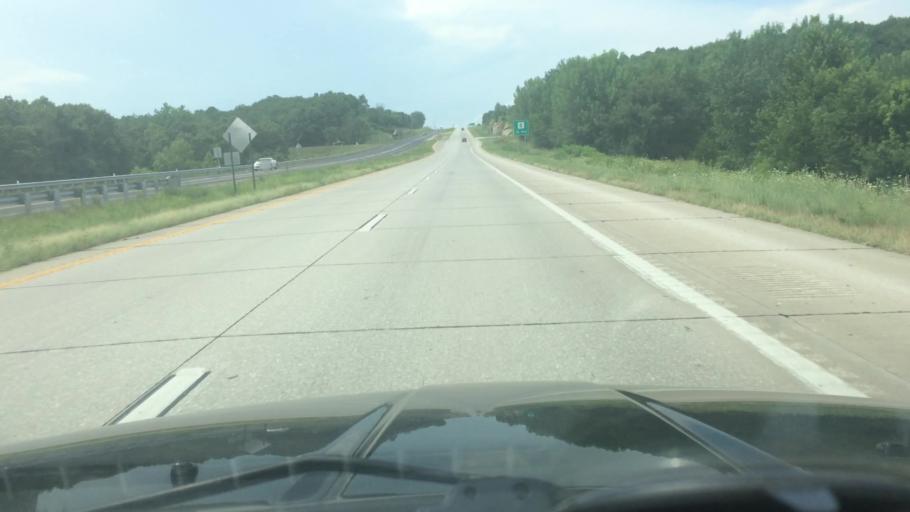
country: US
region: Missouri
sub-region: Saint Clair County
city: Osceola
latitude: 38.0630
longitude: -93.6943
